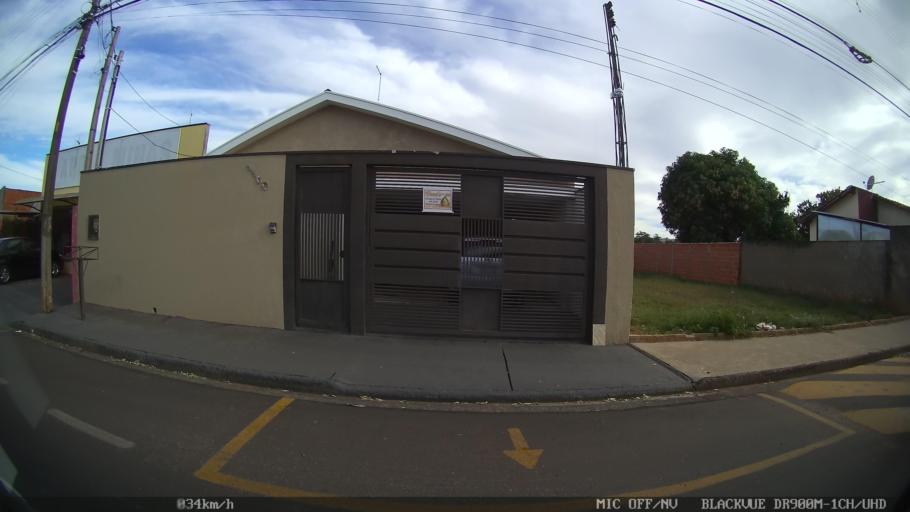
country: BR
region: Sao Paulo
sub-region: Catanduva
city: Catanduva
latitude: -21.1392
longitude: -48.9995
